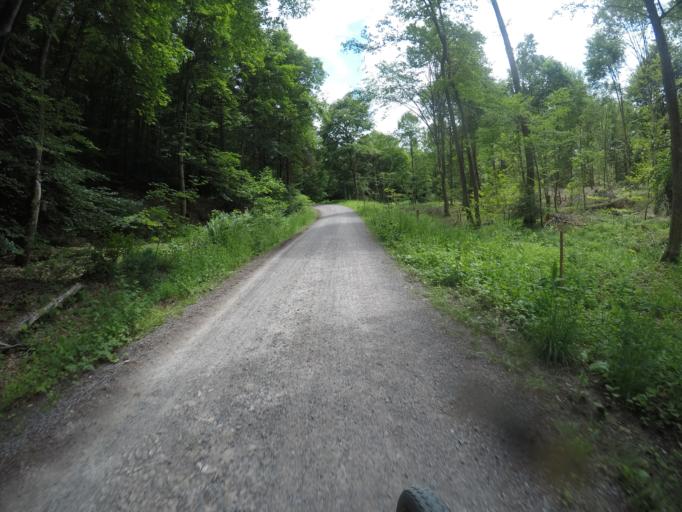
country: DE
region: Baden-Wuerttemberg
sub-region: Regierungsbezirk Stuttgart
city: Hildrizhausen
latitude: 48.5931
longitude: 8.9421
